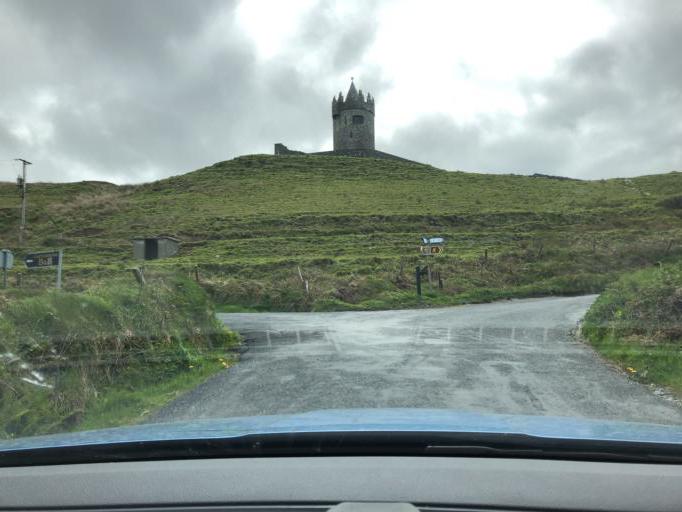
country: IE
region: Connaught
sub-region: County Galway
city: Bearna
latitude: 53.0049
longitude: -9.3879
